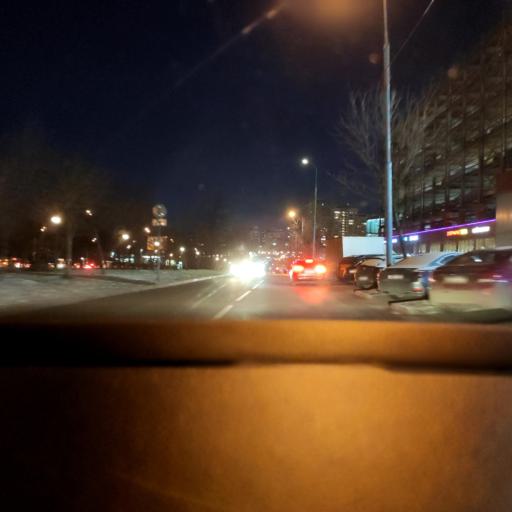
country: RU
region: Moskovskaya
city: Pavshino
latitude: 55.8468
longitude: 37.3734
